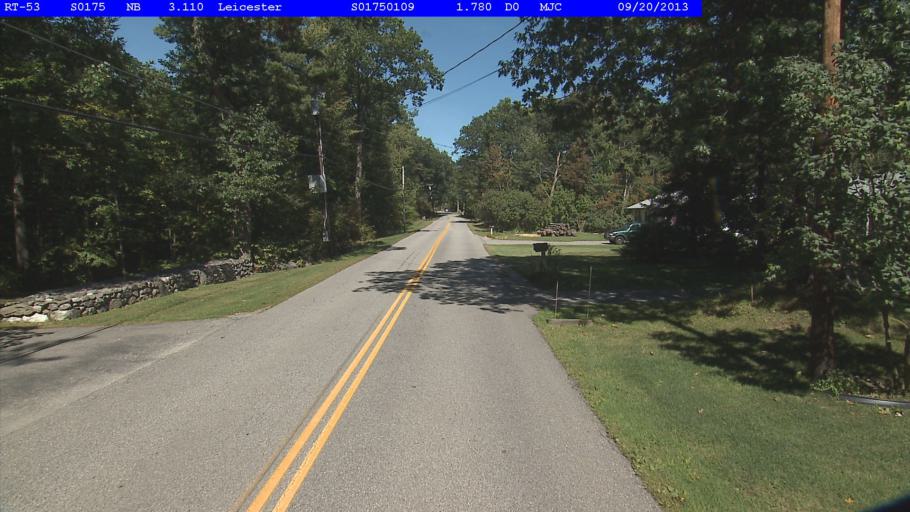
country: US
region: Vermont
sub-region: Rutland County
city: Brandon
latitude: 43.8685
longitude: -73.0652
